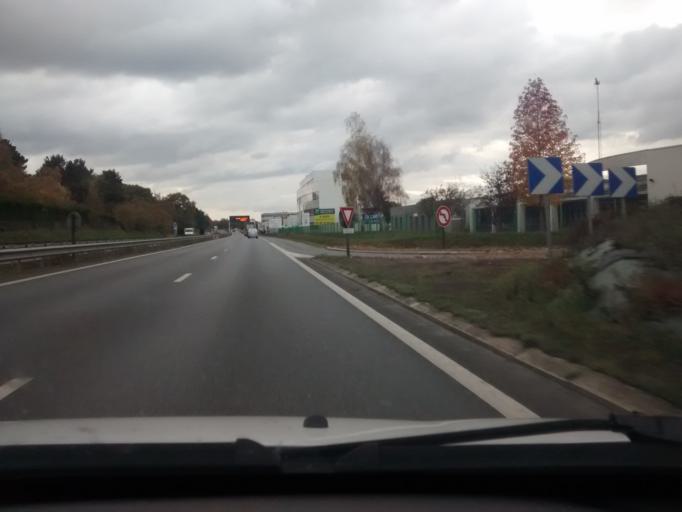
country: FR
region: Brittany
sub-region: Departement d'Ille-et-Vilaine
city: Chantepie
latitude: 48.0734
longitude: -1.6268
